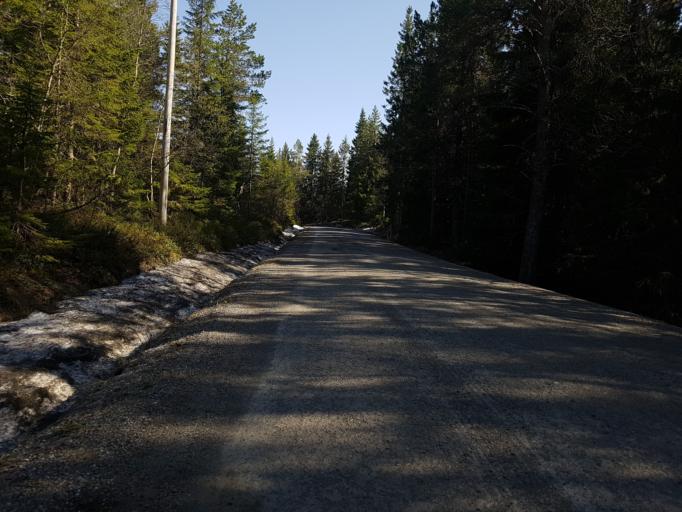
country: NO
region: Sor-Trondelag
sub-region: Trondheim
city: Trondheim
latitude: 63.4262
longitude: 10.2938
